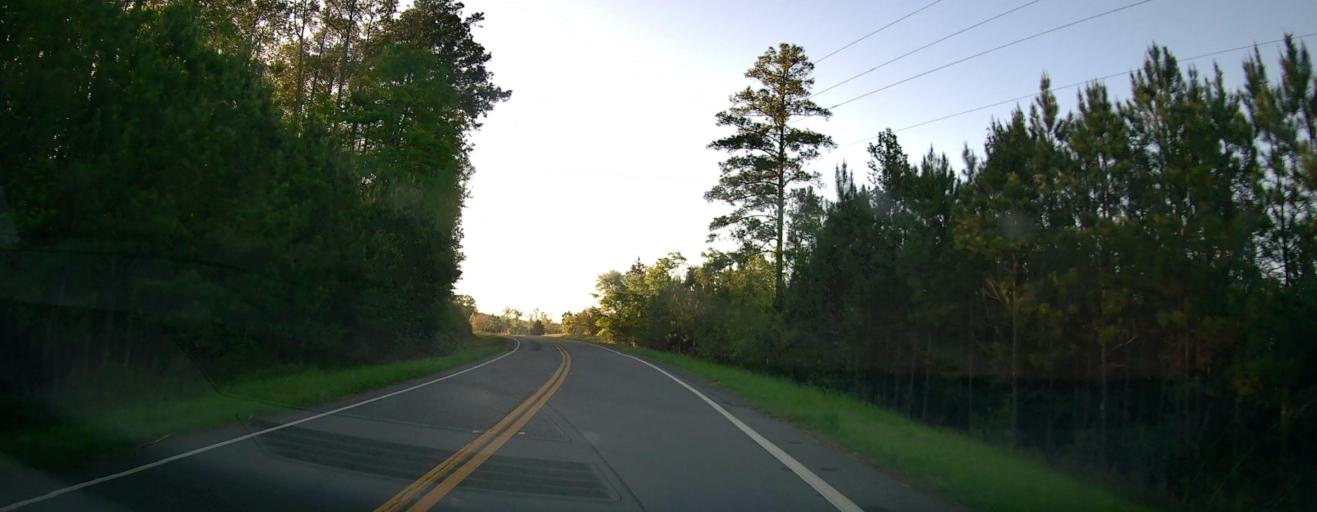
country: US
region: Georgia
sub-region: Macon County
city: Oglethorpe
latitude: 32.3120
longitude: -84.1631
